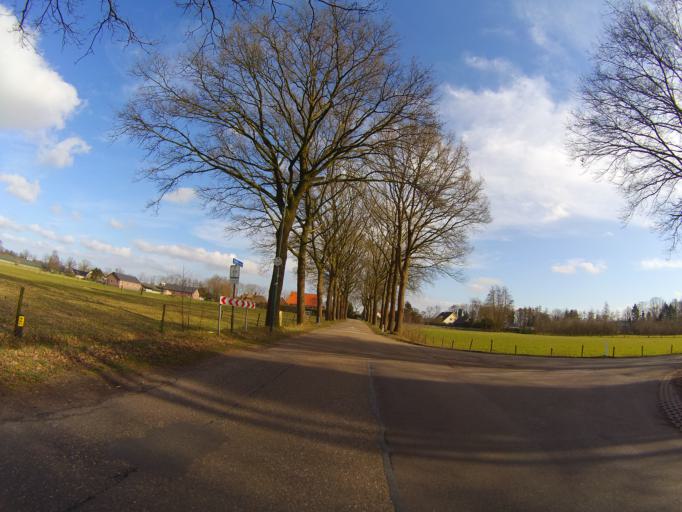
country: NL
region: Gelderland
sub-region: Gemeente Barneveld
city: Terschuur
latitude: 52.1442
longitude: 5.4947
